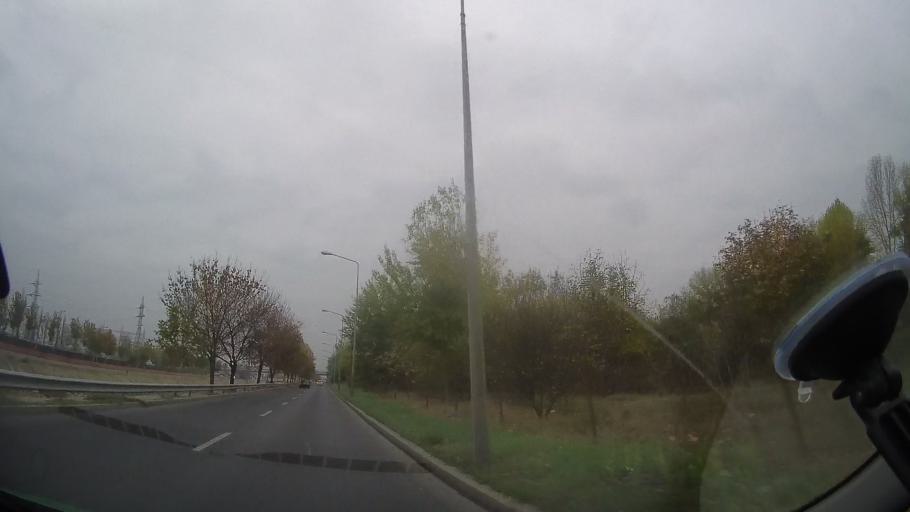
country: RO
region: Ilfov
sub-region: Comuna Popesti-Leordeni
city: Popesti-Leordeni
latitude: 44.4001
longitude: 26.1551
